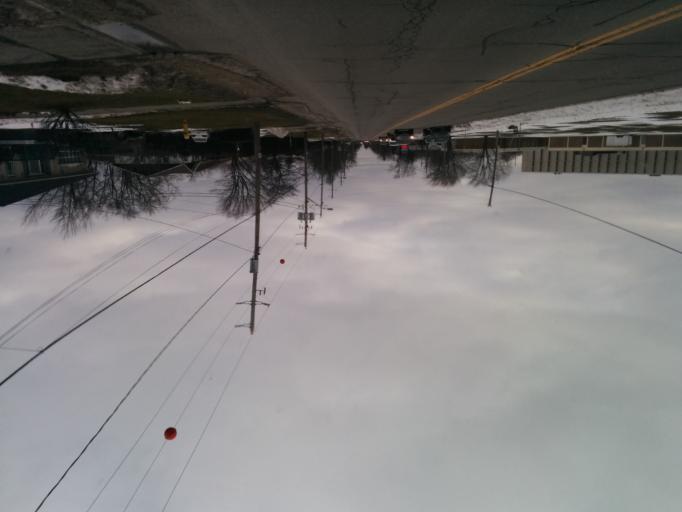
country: CA
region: Ontario
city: Ancaster
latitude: 42.9585
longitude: -80.0418
